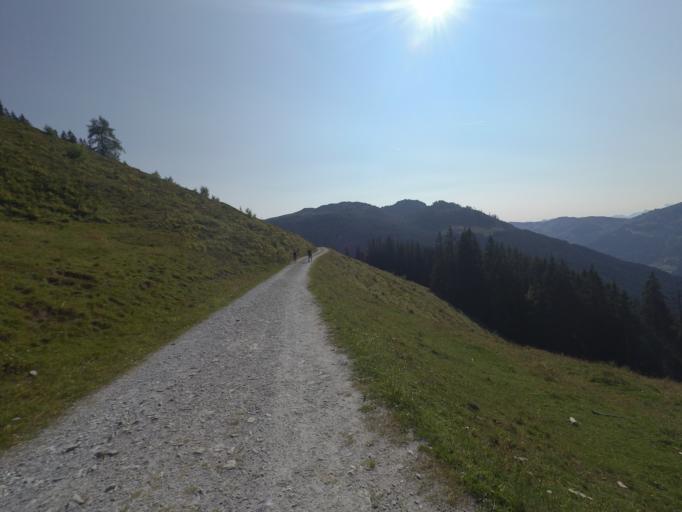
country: AT
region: Salzburg
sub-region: Politischer Bezirk Sankt Johann im Pongau
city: Kleinarl
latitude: 47.2772
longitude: 13.2572
